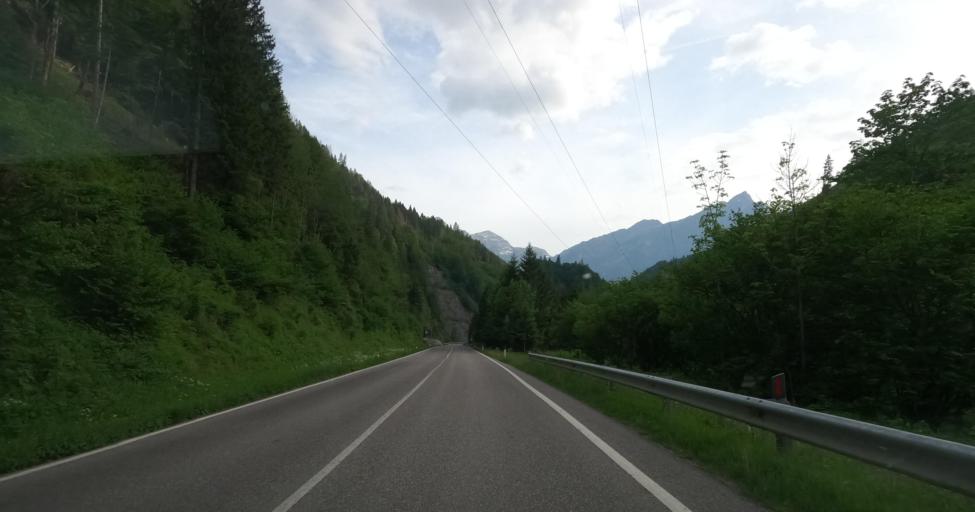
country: IT
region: Veneto
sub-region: Provincia di Belluno
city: Celat-San Tomaso Agordino
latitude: 46.3752
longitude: 11.9820
